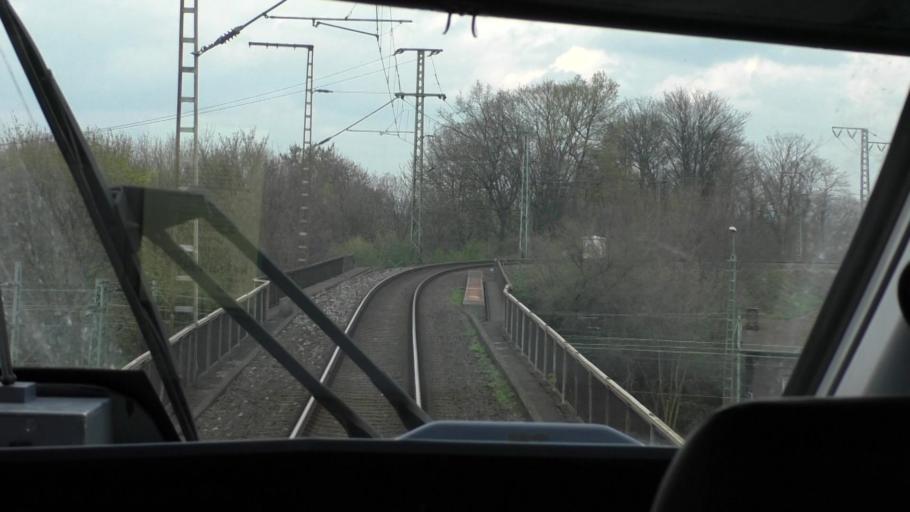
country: DE
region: North Rhine-Westphalia
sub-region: Regierungsbezirk Koln
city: Neustadt/Nord
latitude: 50.9516
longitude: 6.9424
